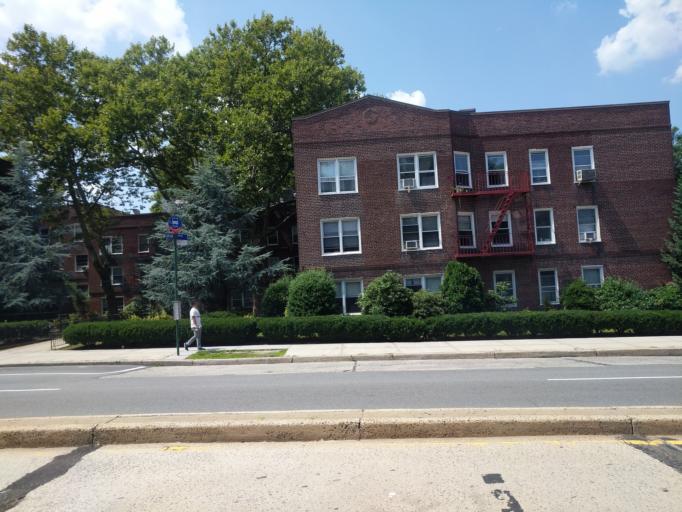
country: US
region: New York
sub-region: Queens County
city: Jamaica
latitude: 40.7191
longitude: -73.8178
